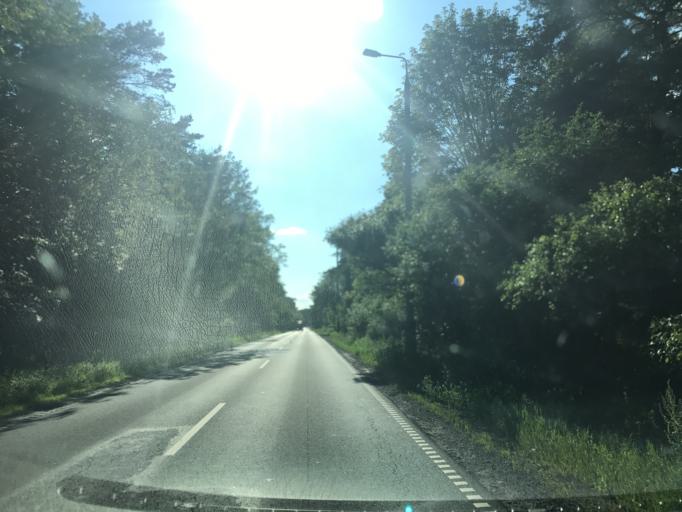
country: PL
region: Kujawsko-Pomorskie
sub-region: Wloclawek
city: Wloclawek
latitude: 52.6344
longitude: 19.0327
